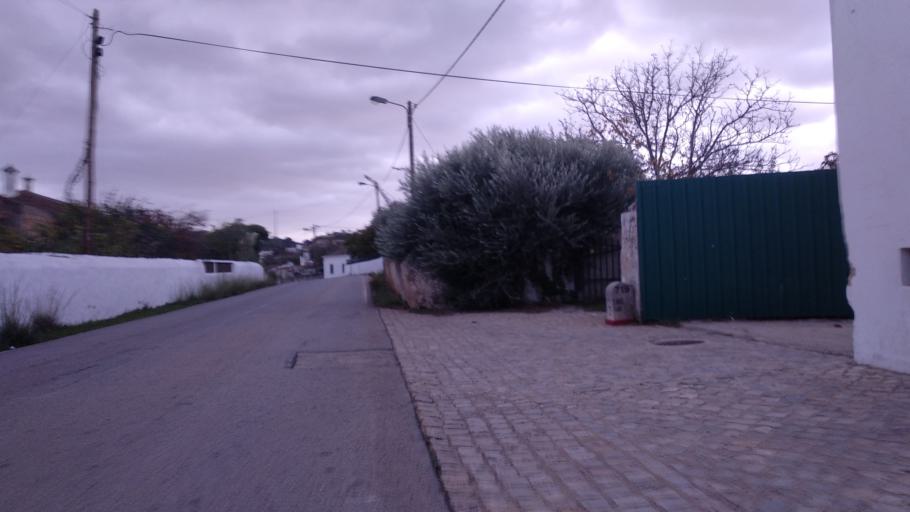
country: PT
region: Faro
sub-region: Sao Bras de Alportel
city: Sao Bras de Alportel
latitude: 37.1710
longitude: -7.9084
